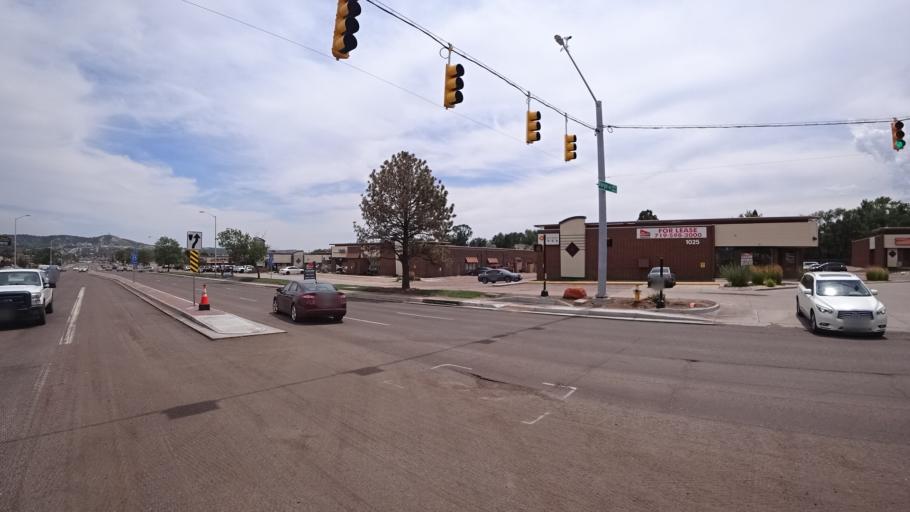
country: US
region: Colorado
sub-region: El Paso County
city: Colorado Springs
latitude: 38.8967
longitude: -104.8409
